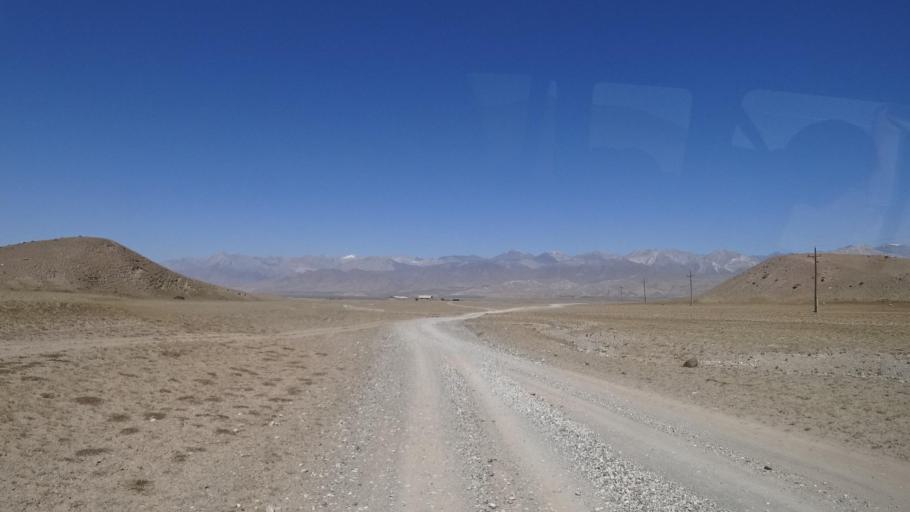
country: KG
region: Osh
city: Gul'cha
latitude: 39.6072
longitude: 72.8769
